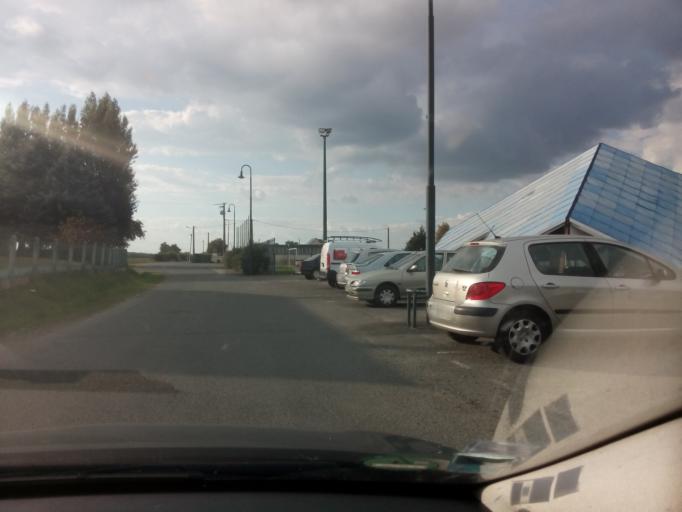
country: FR
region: Pays de la Loire
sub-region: Departement de Maine-et-Loire
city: Soulaire-et-Bourg
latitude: 47.5796
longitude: -0.5548
